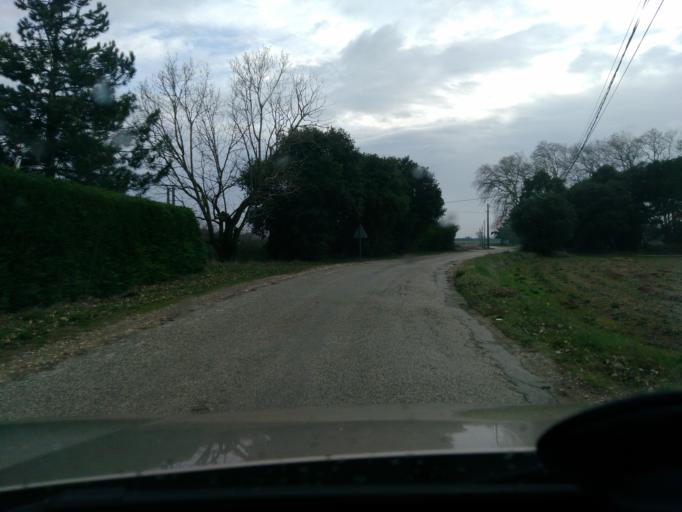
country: FR
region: Rhone-Alpes
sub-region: Departement de la Drome
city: Savasse
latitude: 44.5785
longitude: 4.7750
